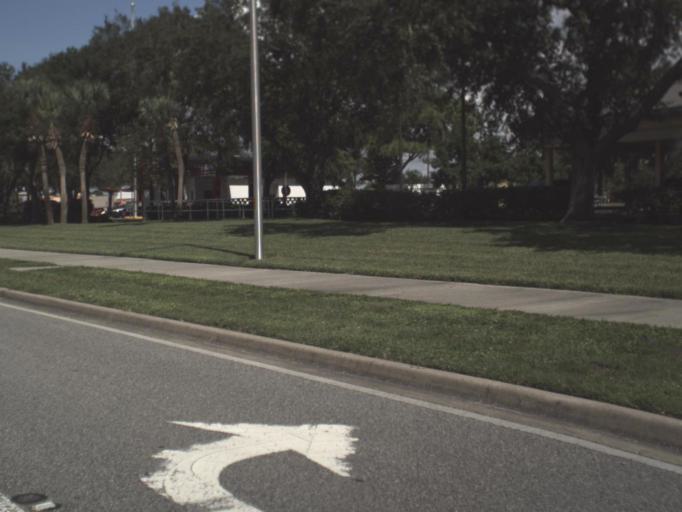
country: US
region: Florida
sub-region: Sarasota County
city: Venice Gardens
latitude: 27.0714
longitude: -82.4229
